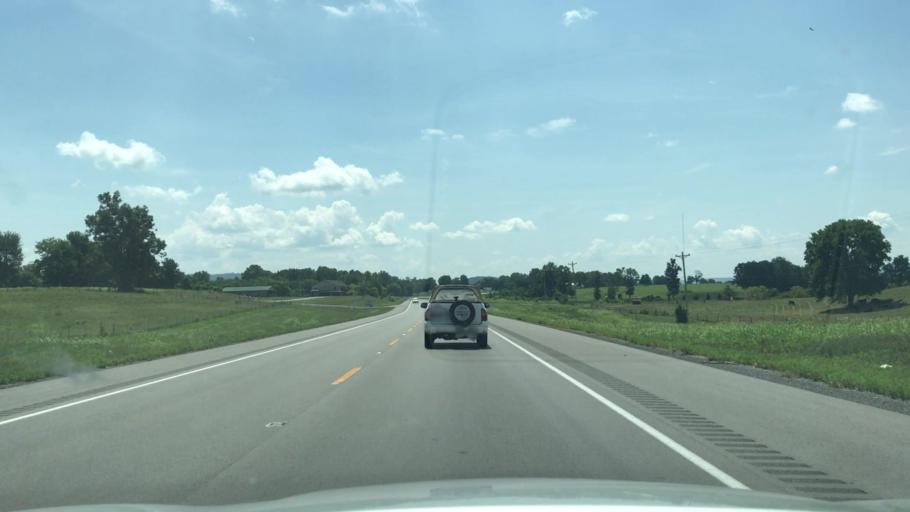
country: US
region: Tennessee
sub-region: Pickett County
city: Byrdstown
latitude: 36.6321
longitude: -85.0954
